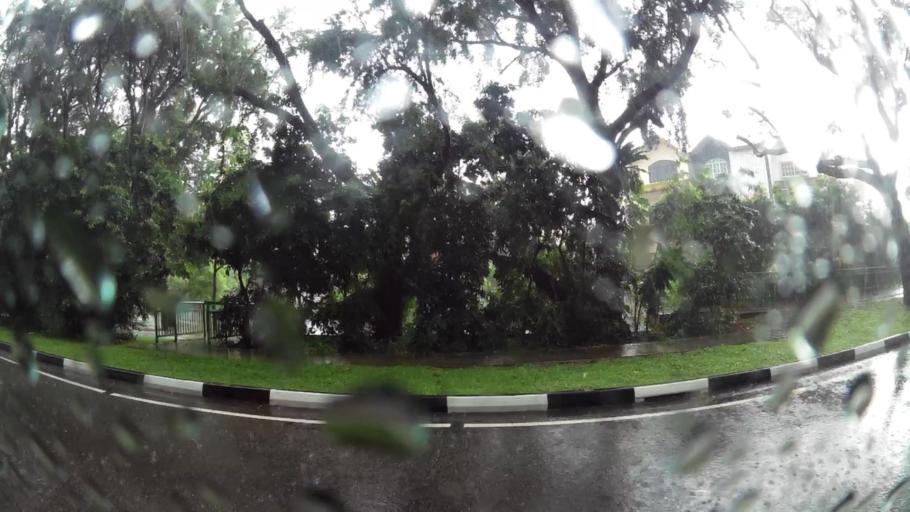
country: SG
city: Singapore
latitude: 1.3255
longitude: 103.9061
